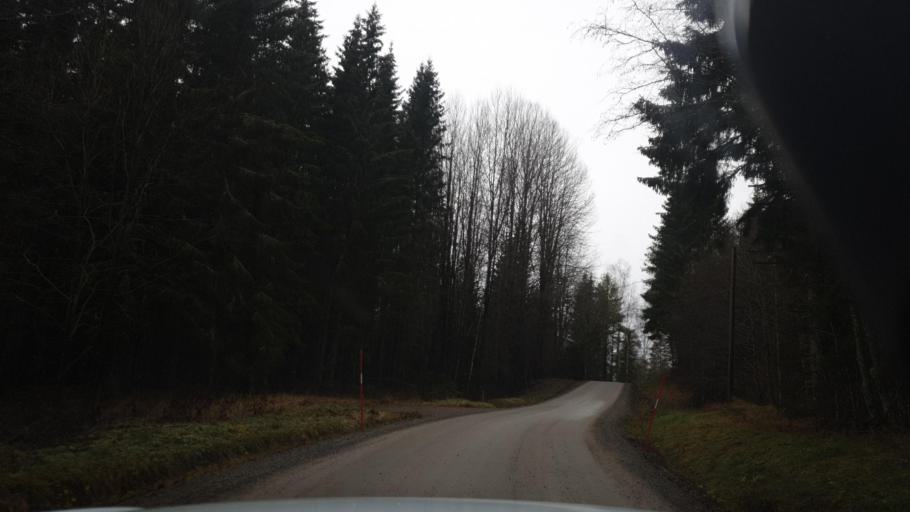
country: SE
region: Vaermland
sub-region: Arvika Kommun
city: Arvika
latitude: 59.7061
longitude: 12.8566
